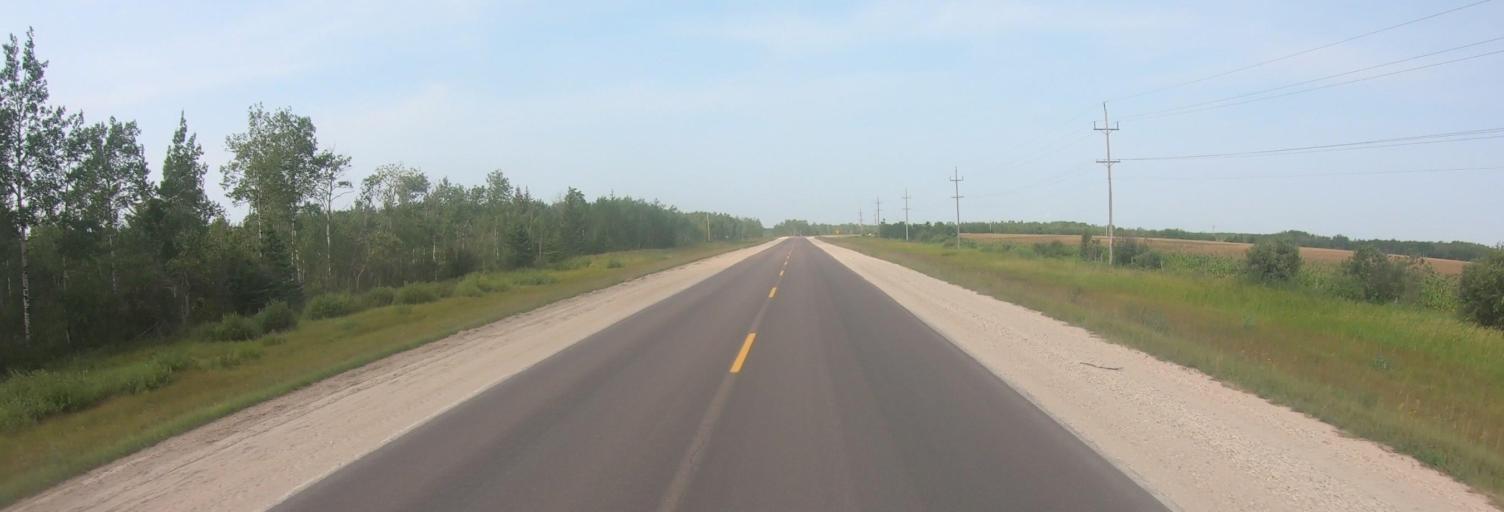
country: CA
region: Manitoba
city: La Broquerie
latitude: 49.2669
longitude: -96.4676
